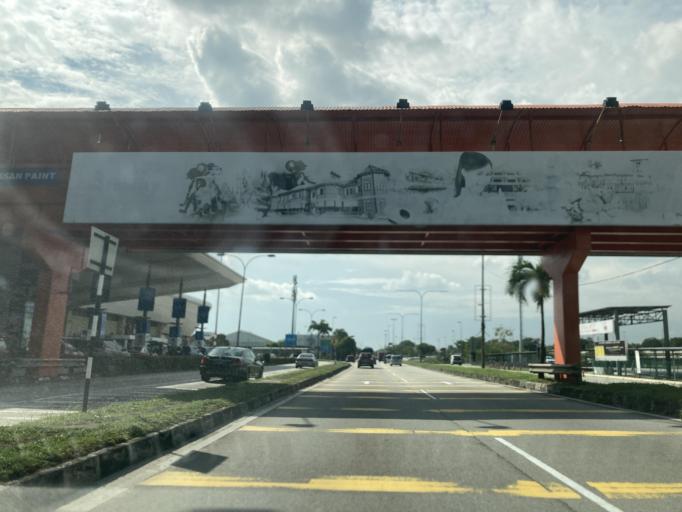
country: MY
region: Selangor
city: Kampung Baru Subang
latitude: 3.1332
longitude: 101.5543
